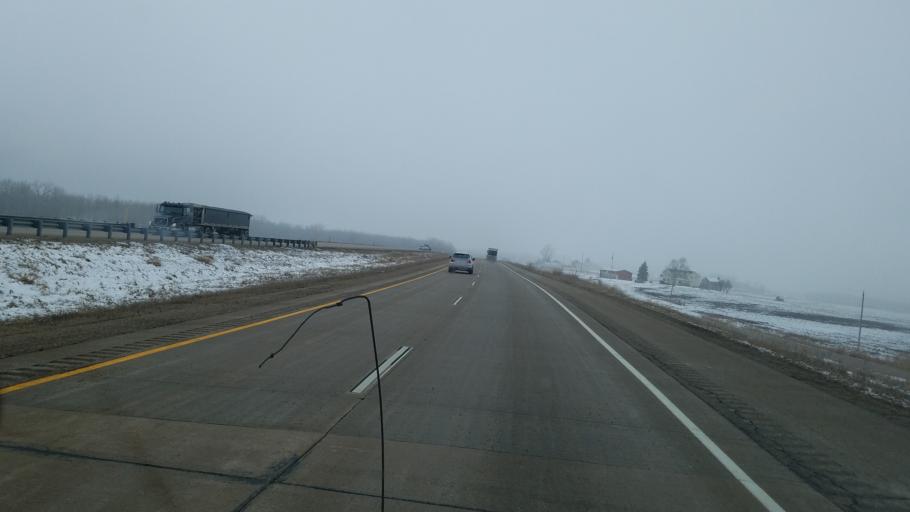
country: US
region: Wisconsin
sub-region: Winnebago County
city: Winneconne
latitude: 44.2244
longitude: -88.7054
